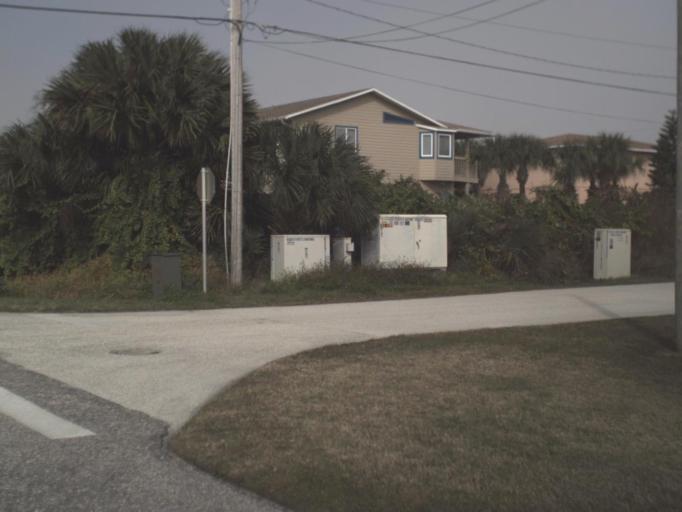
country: US
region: Florida
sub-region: Volusia County
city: Edgewater
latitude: 28.9585
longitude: -80.8455
